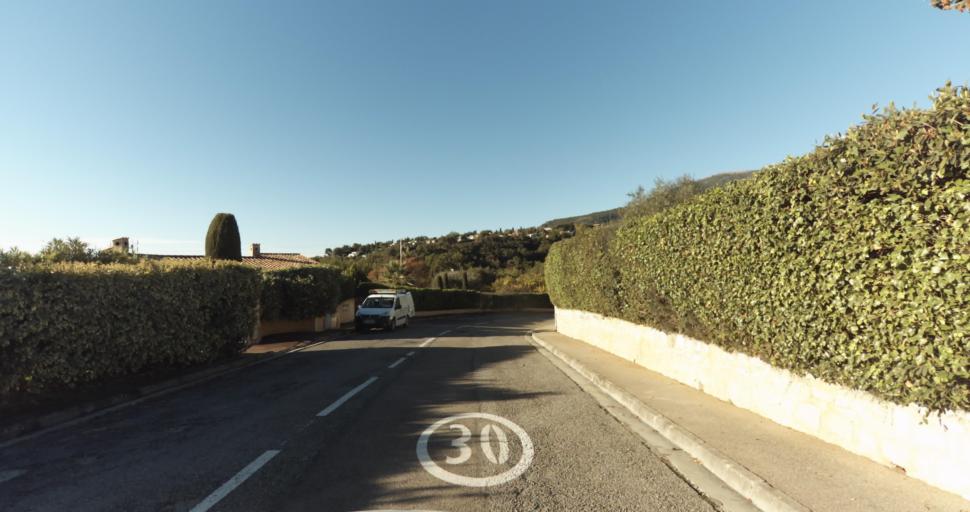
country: FR
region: Provence-Alpes-Cote d'Azur
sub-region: Departement des Alpes-Maritimes
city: Vence
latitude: 43.7236
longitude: 7.0817
